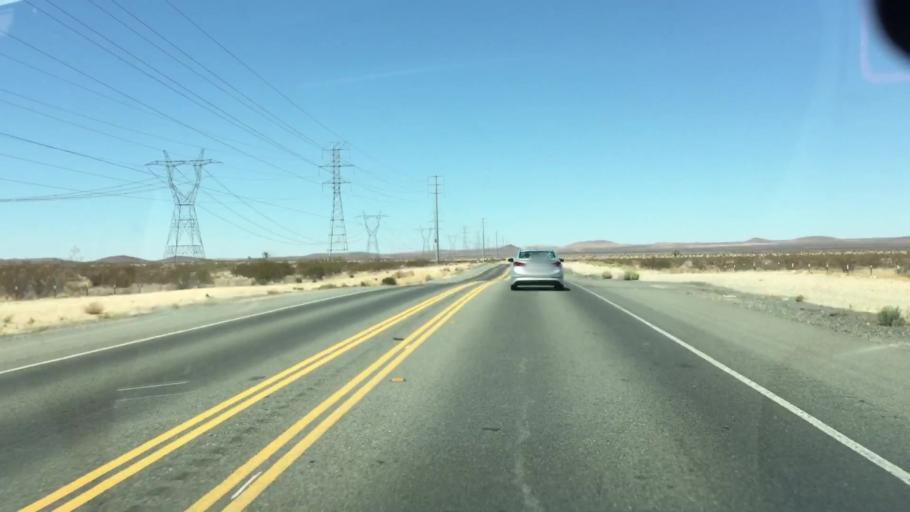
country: US
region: California
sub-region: San Bernardino County
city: Adelanto
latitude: 34.7829
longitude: -117.4815
